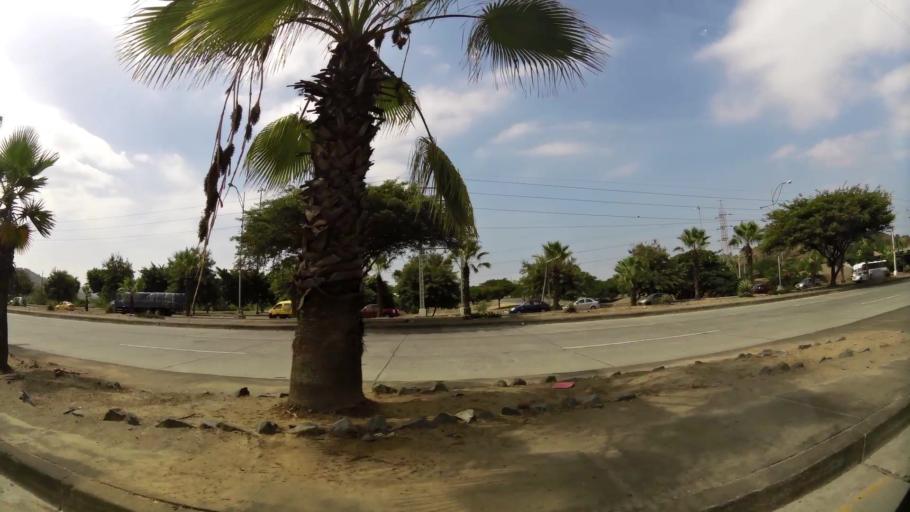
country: EC
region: Guayas
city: Eloy Alfaro
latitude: -2.0735
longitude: -79.9207
